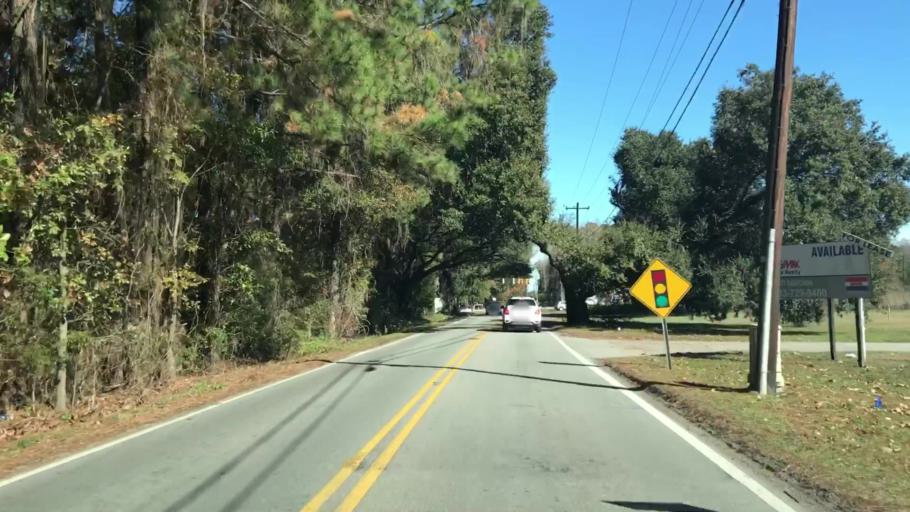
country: US
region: South Carolina
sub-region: Dorchester County
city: Summerville
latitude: 33.0329
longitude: -80.1897
